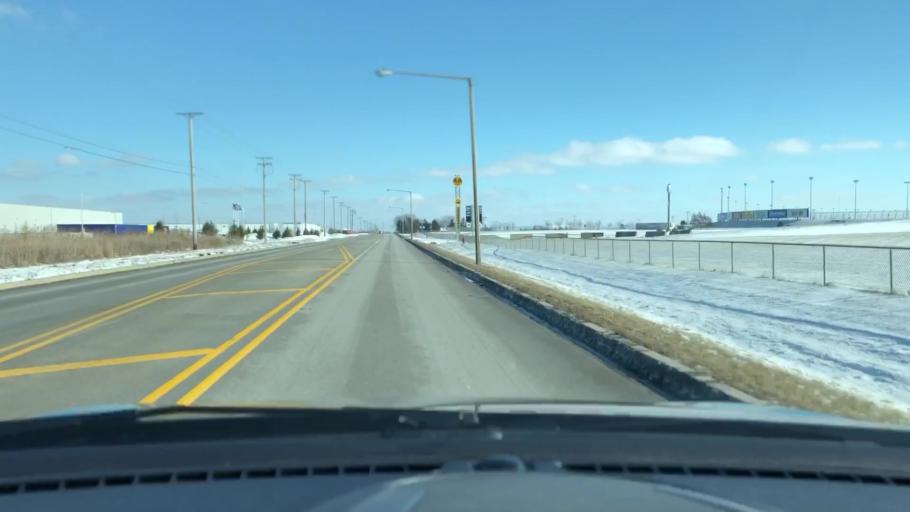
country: US
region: Illinois
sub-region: Will County
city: Preston Heights
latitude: 41.4810
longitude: -88.0660
